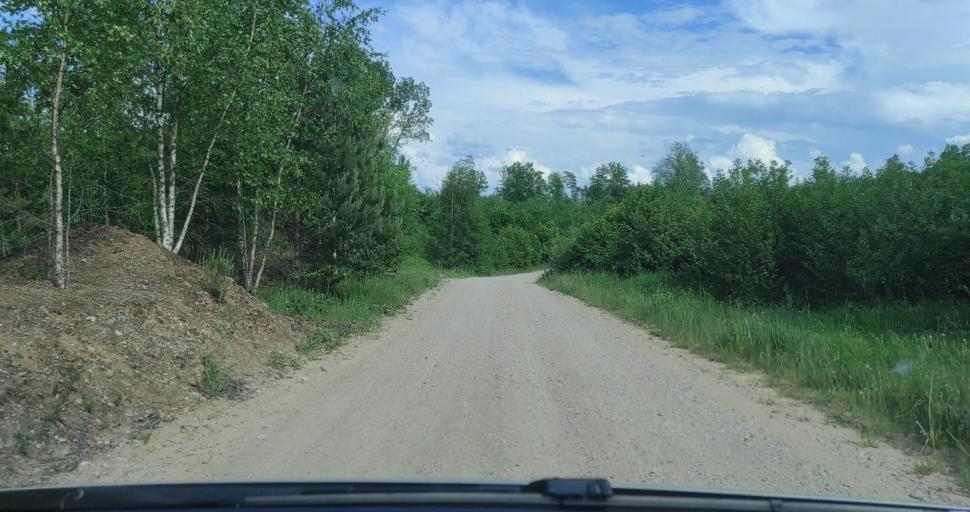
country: LV
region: Kuldigas Rajons
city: Kuldiga
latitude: 56.8600
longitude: 21.9184
